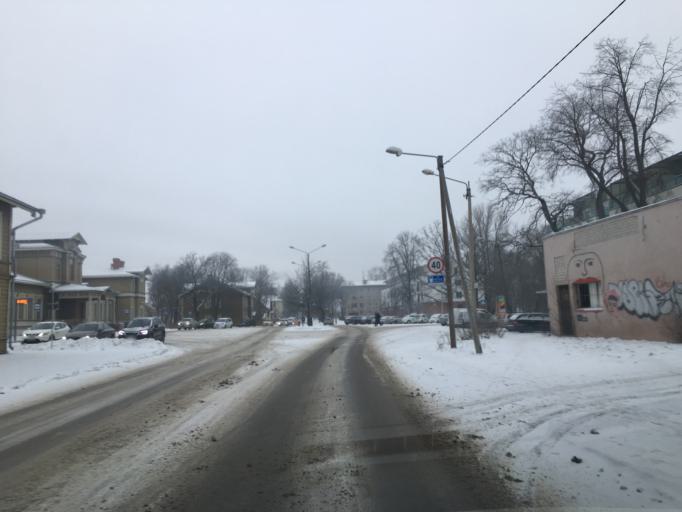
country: EE
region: Tartu
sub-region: Tartu linn
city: Tartu
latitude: 58.3735
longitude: 26.7081
